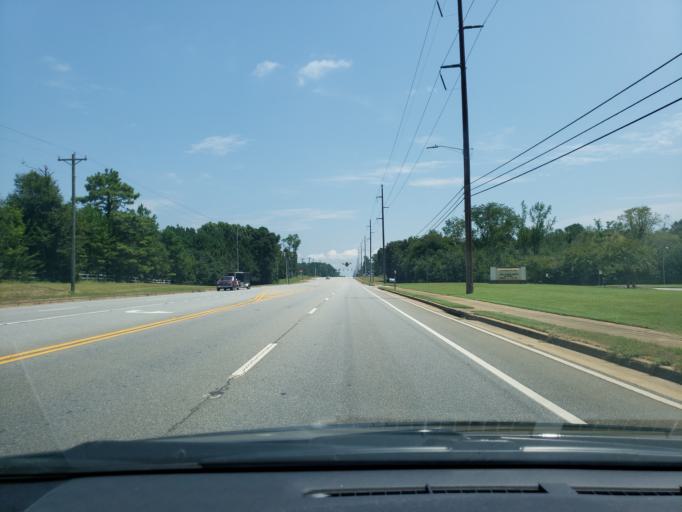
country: US
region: Georgia
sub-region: Dougherty County
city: Albany
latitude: 31.5856
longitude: -84.2562
